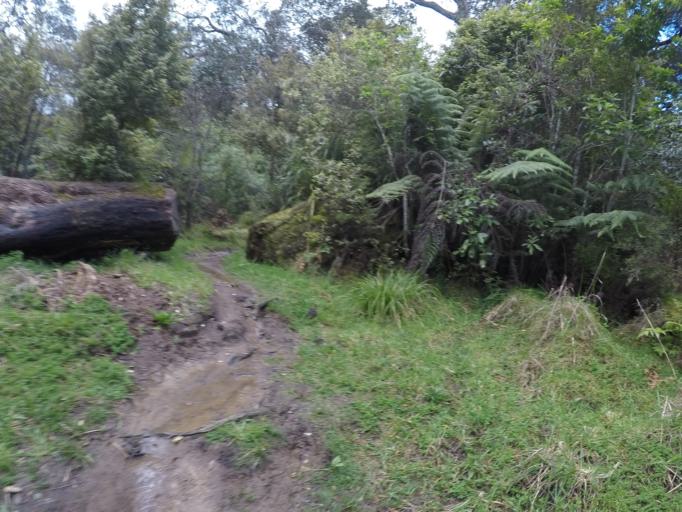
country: NZ
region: Bay of Plenty
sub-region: Western Bay of Plenty District
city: Waihi Beach
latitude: -37.3807
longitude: 175.9364
